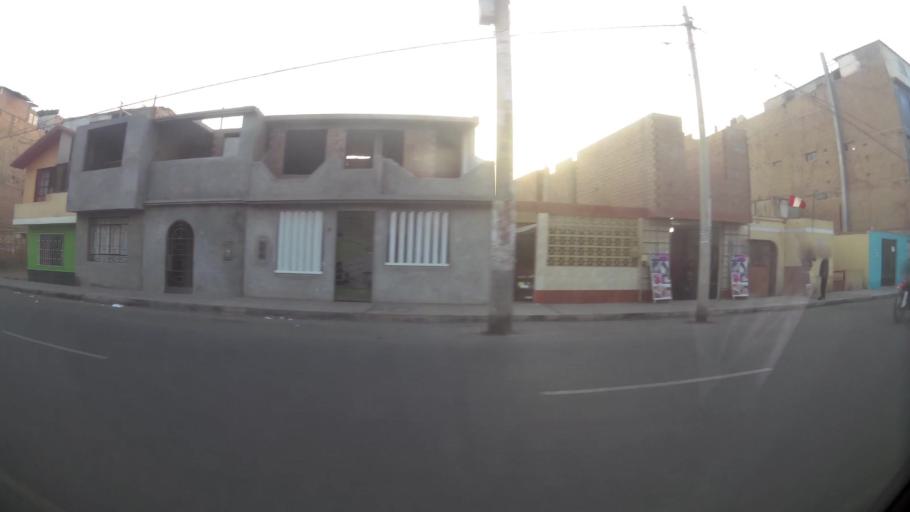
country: PE
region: Lima
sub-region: Huaura
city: Huacho
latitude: -11.1179
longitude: -77.6105
